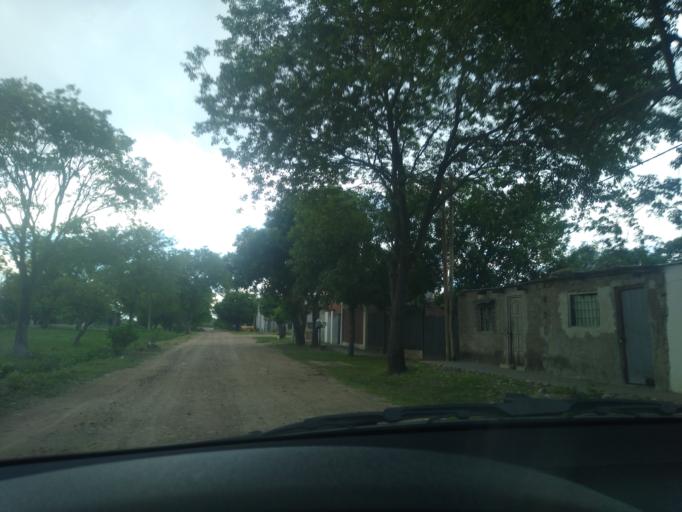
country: AR
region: Chaco
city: Barranqueras
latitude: -27.4889
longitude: -58.9523
